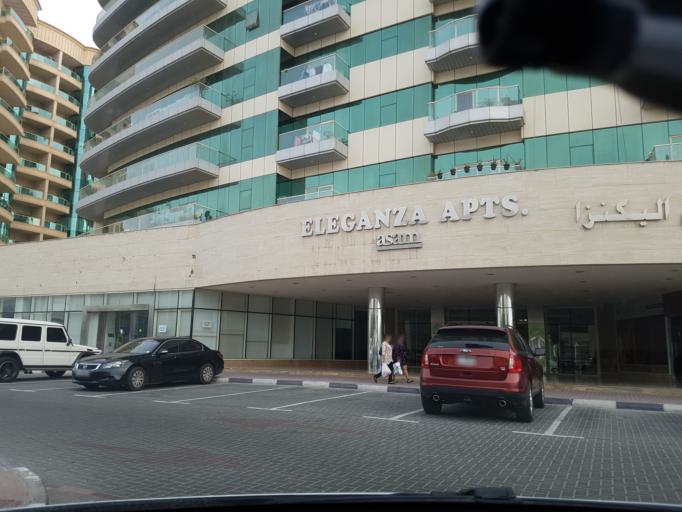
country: AE
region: Ash Shariqah
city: Sharjah
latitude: 25.2343
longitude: 55.3125
